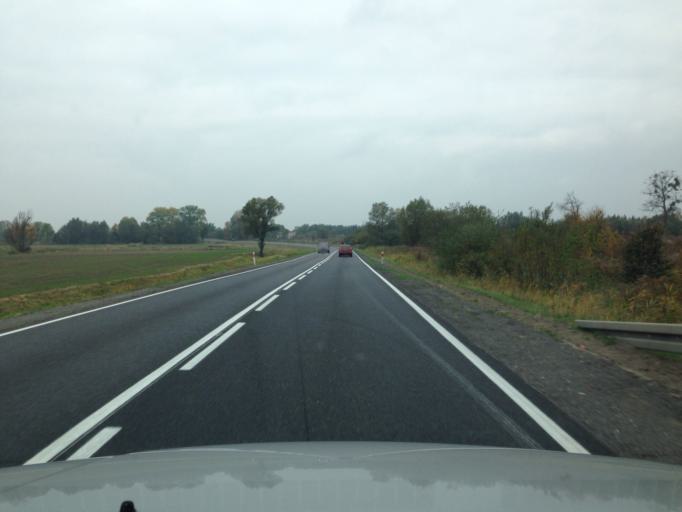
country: PL
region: Warmian-Masurian Voivodeship
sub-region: Powiat elblaski
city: Gronowo Elblaskie
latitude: 54.1350
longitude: 19.3352
